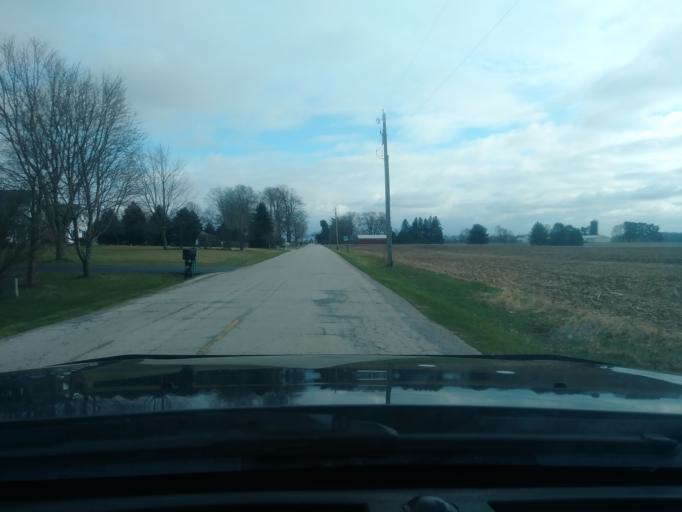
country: US
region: Indiana
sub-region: LaPorte County
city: LaPorte
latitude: 41.5714
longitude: -86.7982
